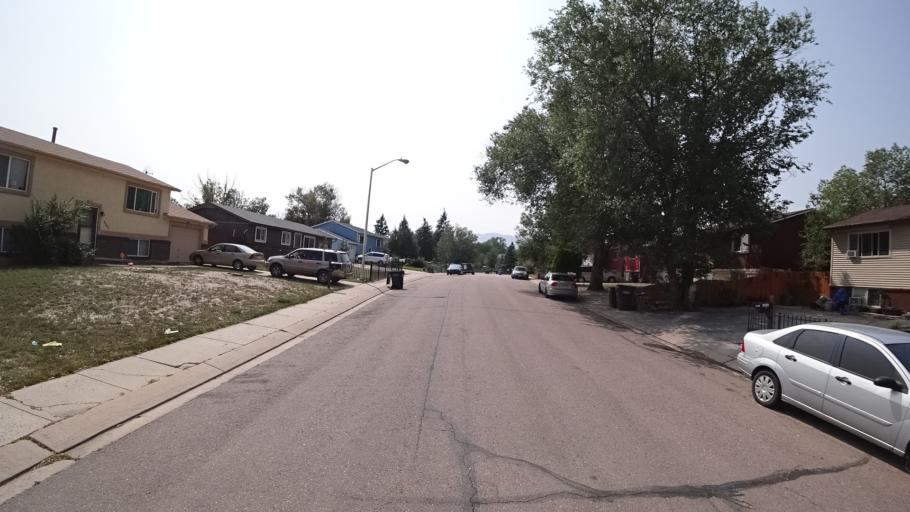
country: US
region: Colorado
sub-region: El Paso County
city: Stratmoor
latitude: 38.8062
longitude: -104.7634
